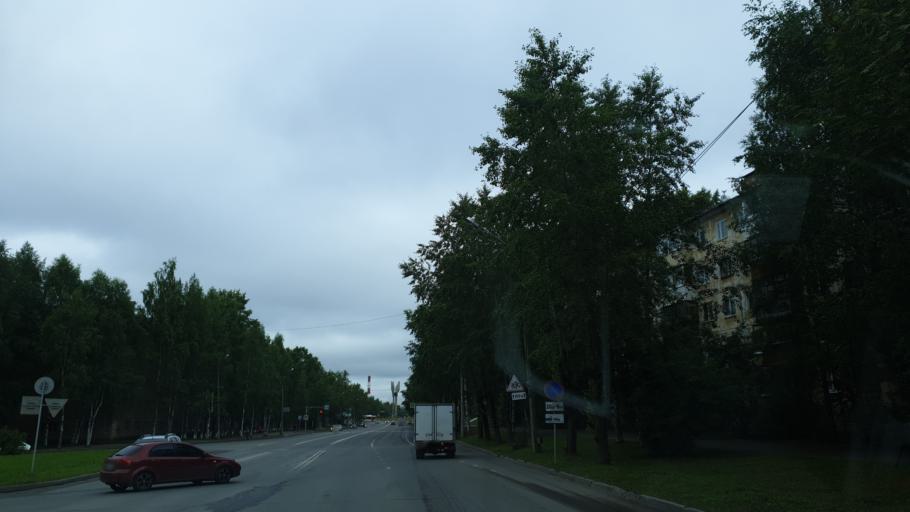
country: RU
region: Komi Republic
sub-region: Syktyvdinskiy Rayon
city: Syktyvkar
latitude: 61.6604
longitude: 50.8197
